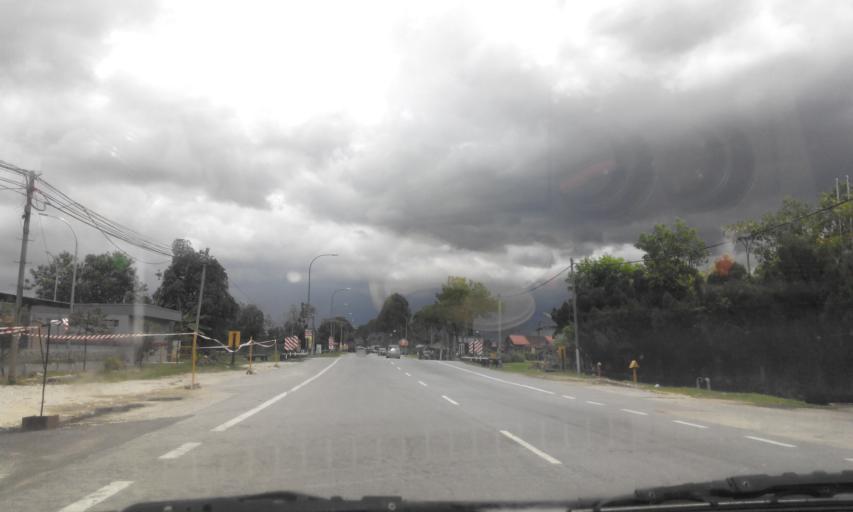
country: MY
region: Perak
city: Parit Buntar
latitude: 5.1086
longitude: 100.4891
